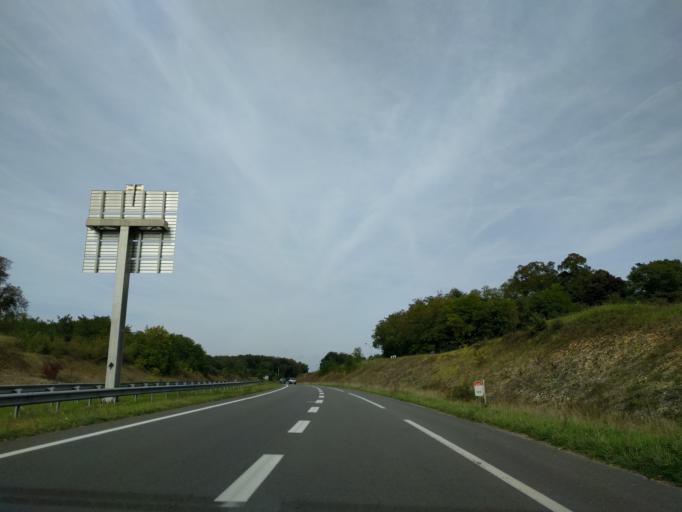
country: FR
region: Centre
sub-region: Departement du Cher
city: Bourges
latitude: 47.0606
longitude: 2.4312
